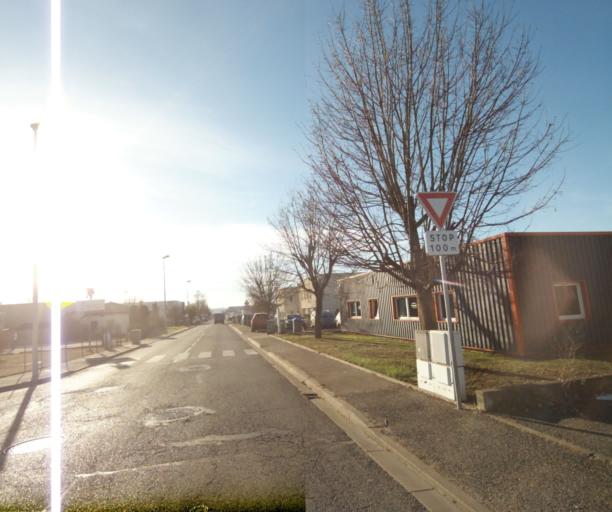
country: FR
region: Lorraine
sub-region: Departement de Meurthe-et-Moselle
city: Pulnoy
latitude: 48.7071
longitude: 6.2513
